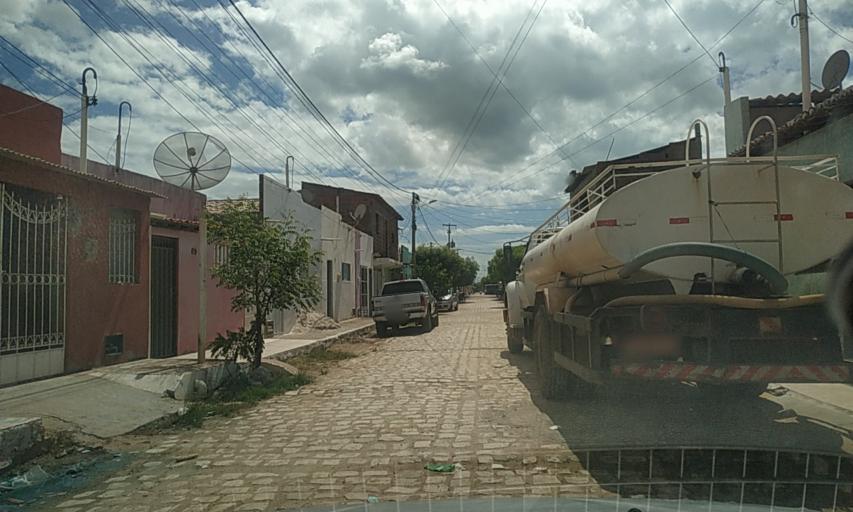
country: BR
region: Rio Grande do Norte
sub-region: Areia Branca
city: Areia Branca
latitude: -4.9519
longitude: -37.1197
